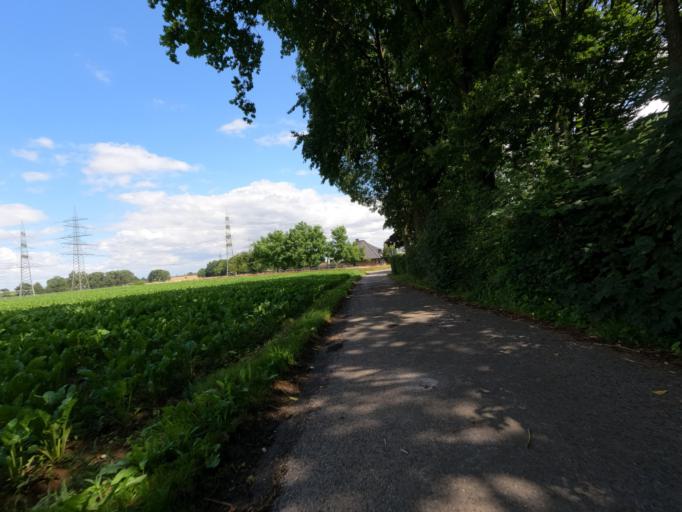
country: DE
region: North Rhine-Westphalia
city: Baesweiler
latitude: 50.9412
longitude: 6.2104
